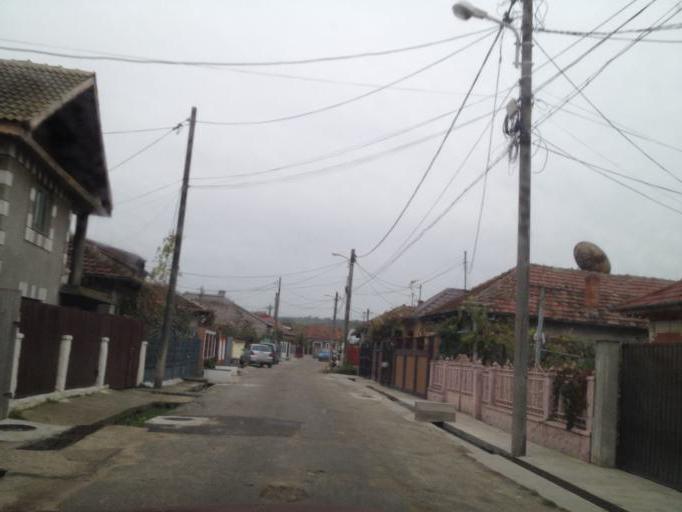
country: RO
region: Dolj
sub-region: Municipiul Craiova
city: Mofleni
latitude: 44.2990
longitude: 23.7612
